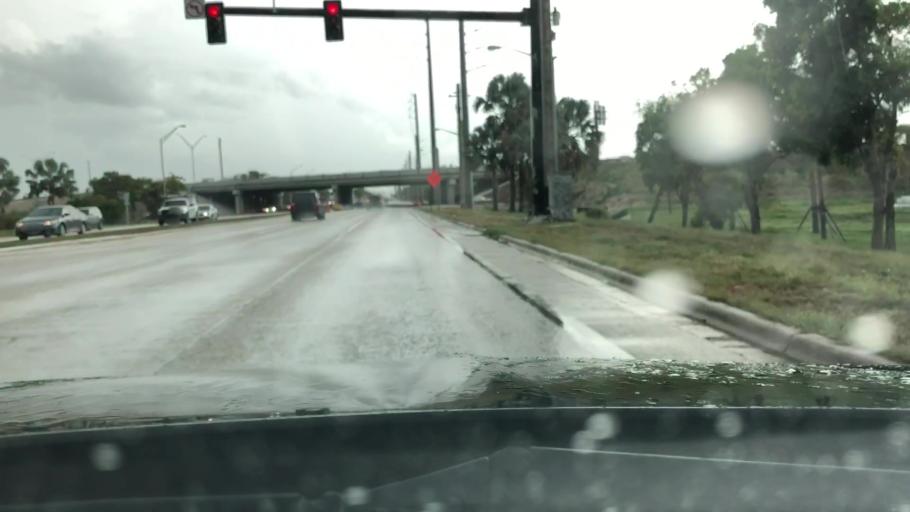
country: US
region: Florida
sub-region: Broward County
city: Kendall Green
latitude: 26.2605
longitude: -80.1311
